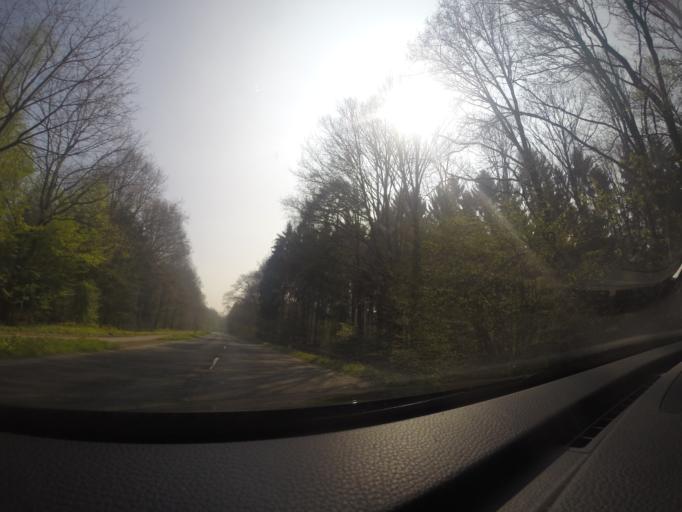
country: DE
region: North Rhine-Westphalia
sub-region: Regierungsbezirk Munster
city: Isselburg
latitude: 51.8391
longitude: 6.4217
